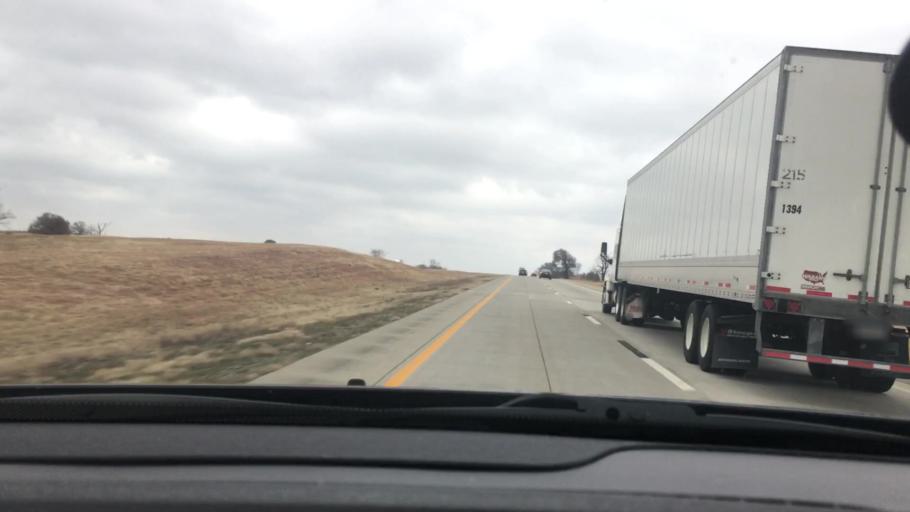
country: US
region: Oklahoma
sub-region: Atoka County
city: Atoka
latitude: 34.2196
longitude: -96.2287
